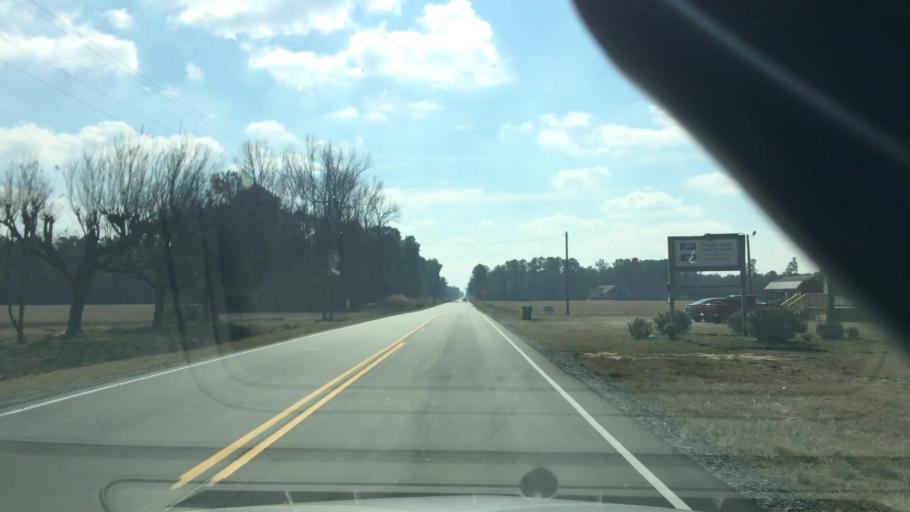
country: US
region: North Carolina
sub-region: Duplin County
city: Beulaville
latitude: 35.0292
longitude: -77.7482
